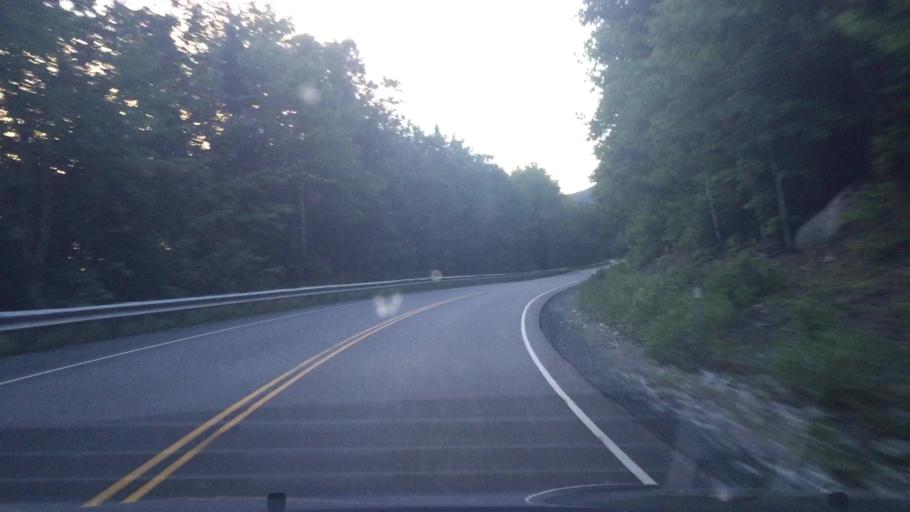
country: US
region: New Hampshire
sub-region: Grafton County
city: Woodstock
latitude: 44.0348
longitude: -71.5195
